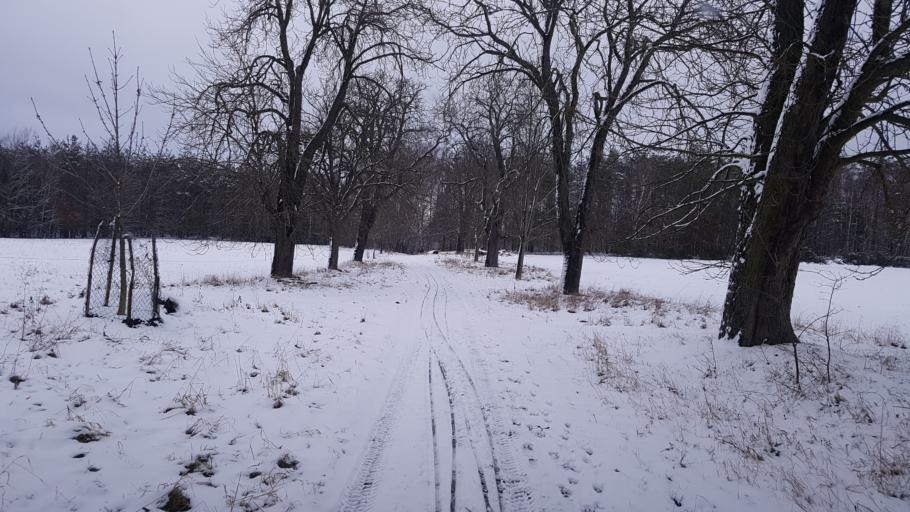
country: DE
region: Brandenburg
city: Crinitz
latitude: 51.7331
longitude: 13.7671
